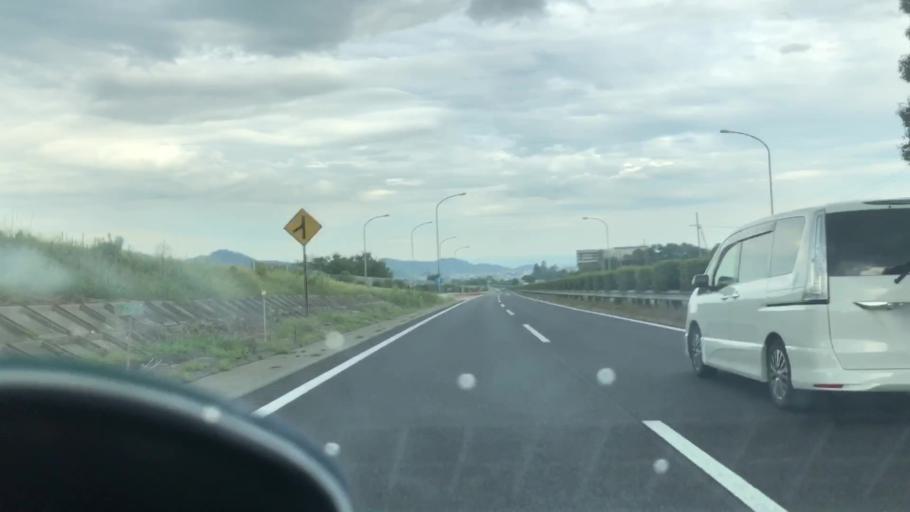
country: JP
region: Hyogo
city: Ono
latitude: 34.9464
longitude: 134.8036
